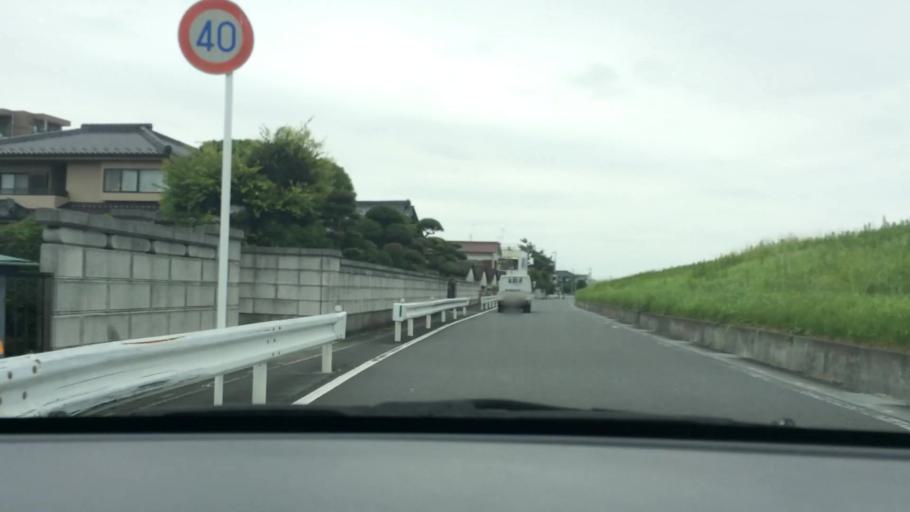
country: JP
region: Chiba
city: Matsudo
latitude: 35.7922
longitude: 139.8865
